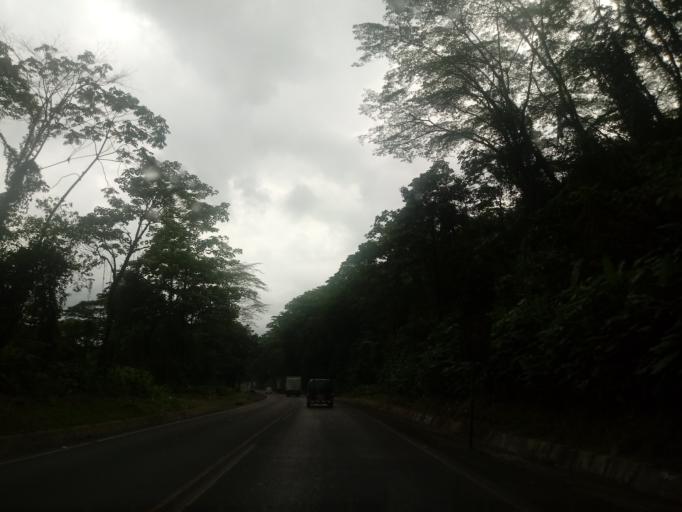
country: CR
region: San Jose
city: Dulce Nombre de Jesus
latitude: 10.1489
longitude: -83.9438
